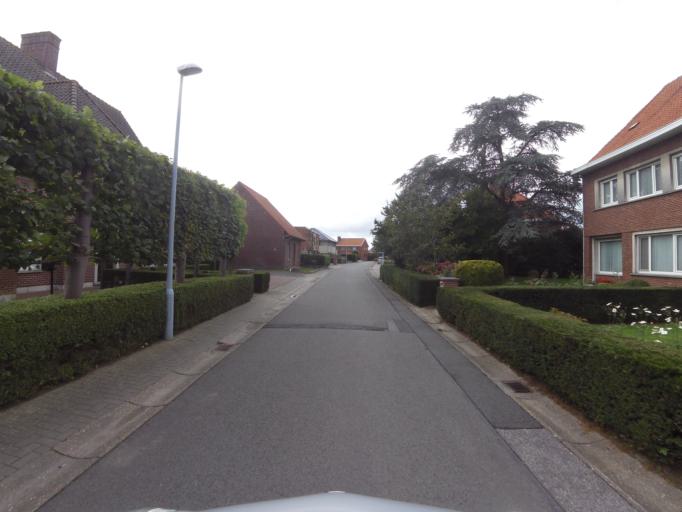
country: BE
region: Flanders
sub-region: Provincie West-Vlaanderen
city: Wingene
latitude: 51.0548
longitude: 3.2772
